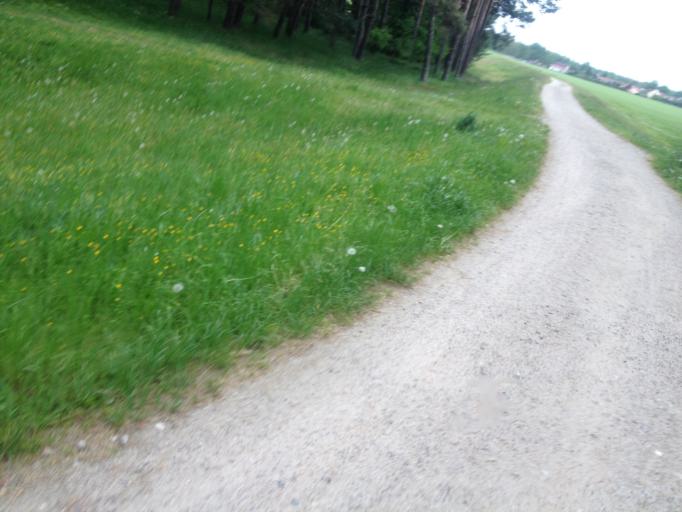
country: DE
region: Brandenburg
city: Drehnow
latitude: 51.8157
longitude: 14.3510
